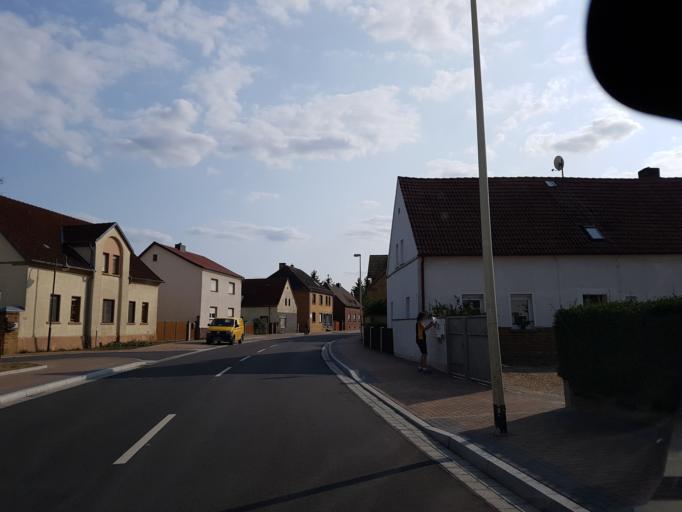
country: DE
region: Saxony-Anhalt
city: Pretzsch
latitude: 51.7507
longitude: 12.7500
